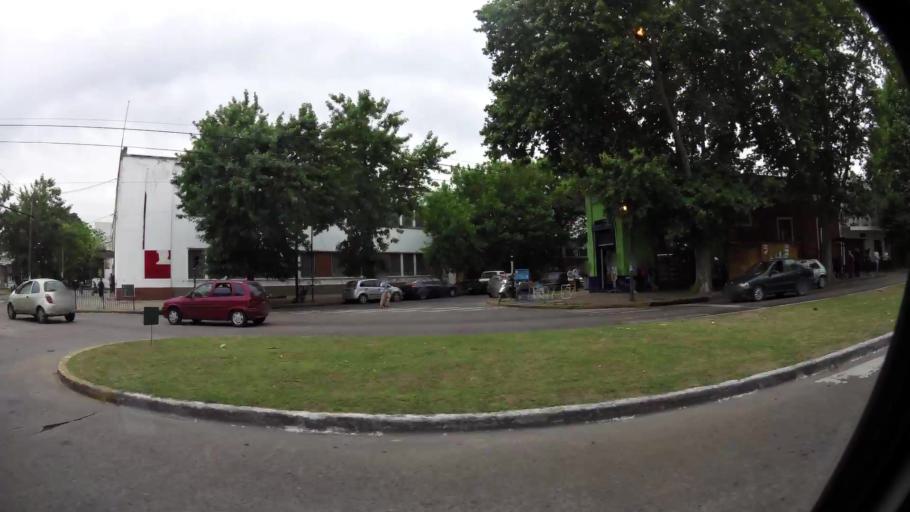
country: AR
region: Buenos Aires
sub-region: Partido de La Plata
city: La Plata
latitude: -34.9378
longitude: -57.9537
